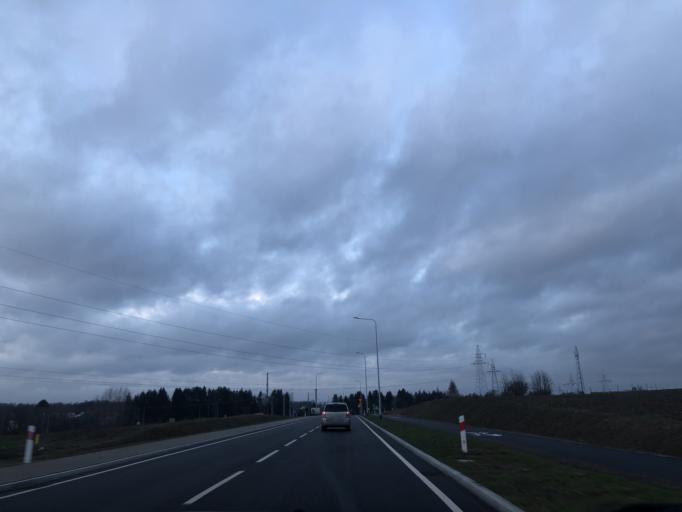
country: PL
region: Podlasie
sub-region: Lomza
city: Lomza
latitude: 53.1492
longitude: 22.0514
